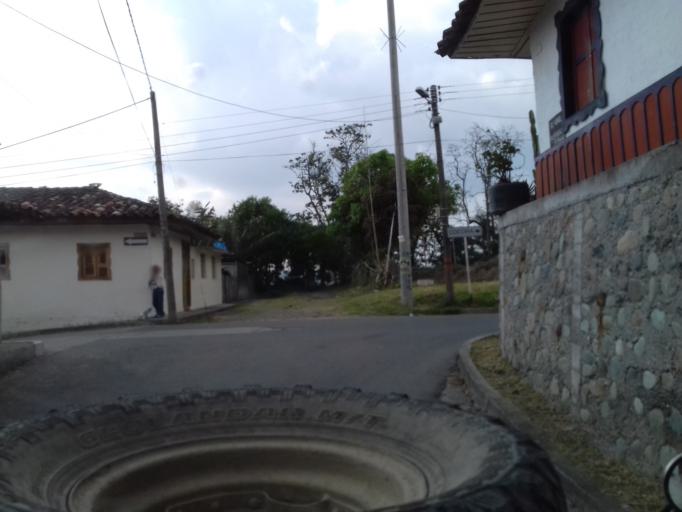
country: CO
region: Quindio
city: Salento
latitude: 4.6409
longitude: -75.5697
